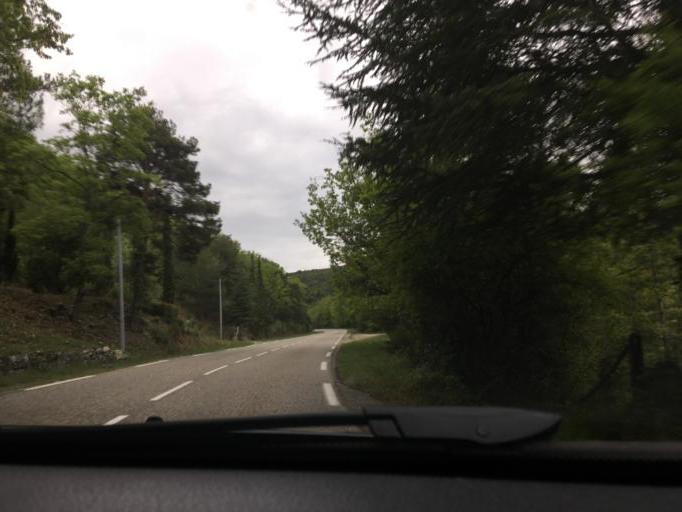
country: FR
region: Provence-Alpes-Cote d'Azur
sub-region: Departement du Var
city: Aups
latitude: 43.7016
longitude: 6.1996
